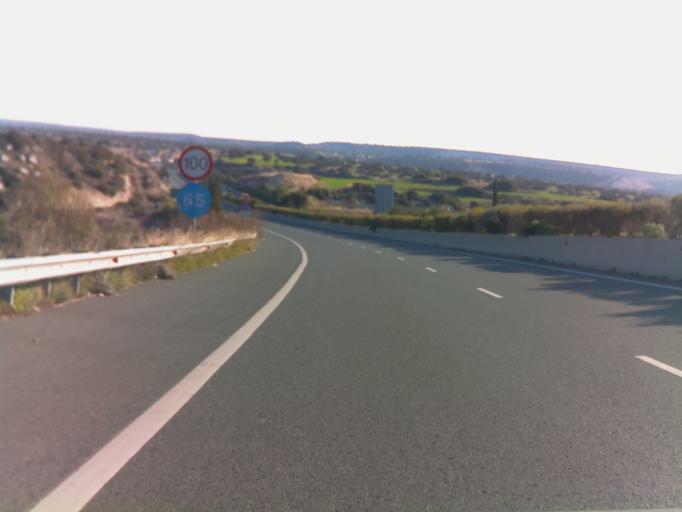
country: CY
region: Limassol
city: Pissouri
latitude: 34.6823
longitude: 32.7679
